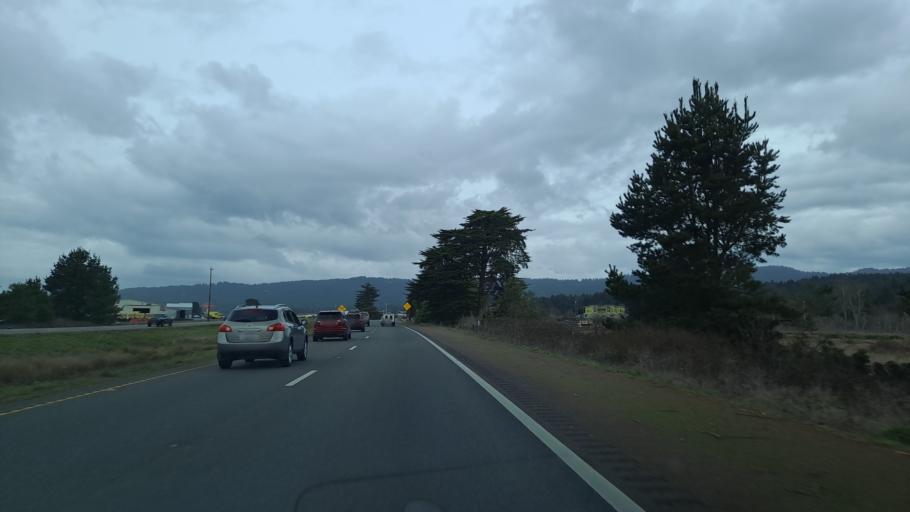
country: US
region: California
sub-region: Humboldt County
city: Bayside
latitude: 40.8240
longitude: -124.0869
